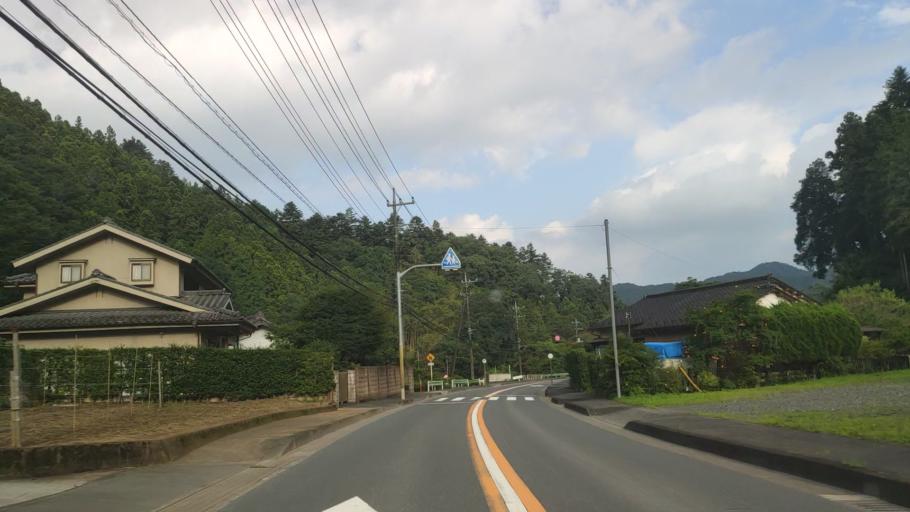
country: JP
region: Tokyo
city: Ome
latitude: 35.8278
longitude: 139.2424
